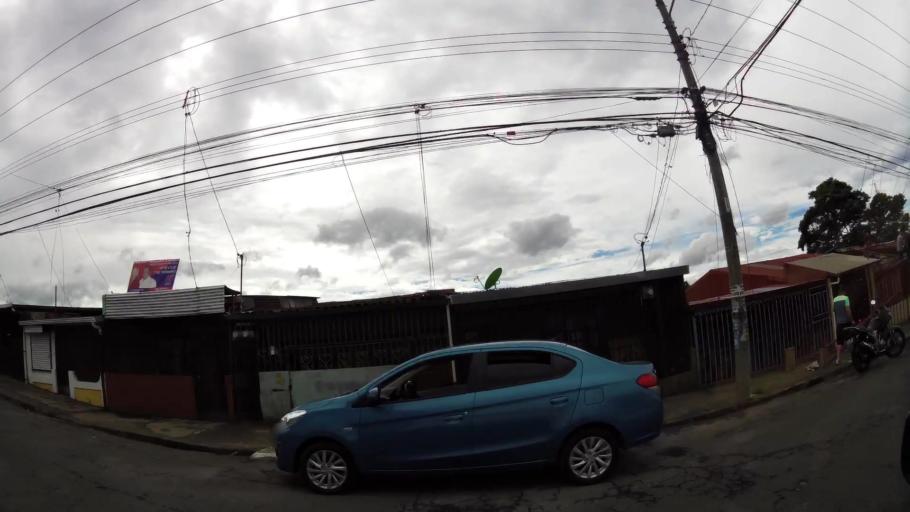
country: CR
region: San Jose
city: Purral
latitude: 9.9617
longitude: -84.0257
